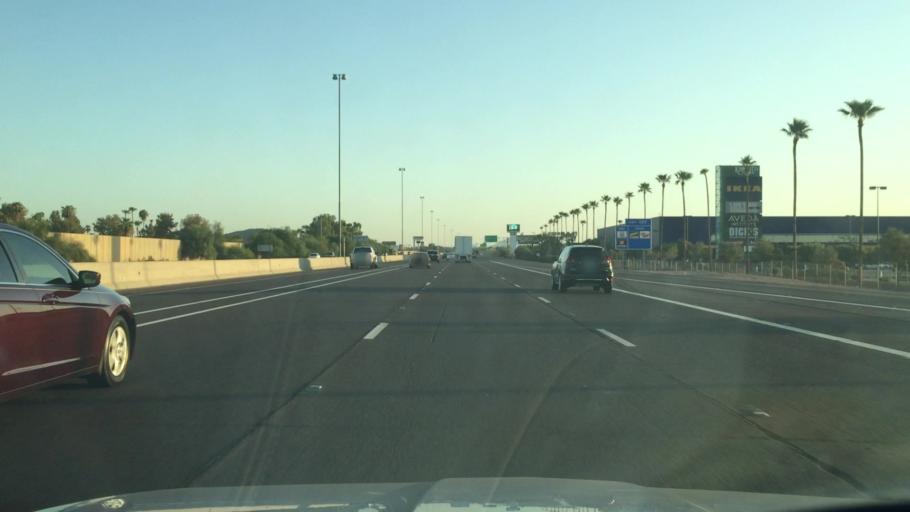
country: US
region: Arizona
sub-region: Maricopa County
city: Guadalupe
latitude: 33.3382
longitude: -111.9734
